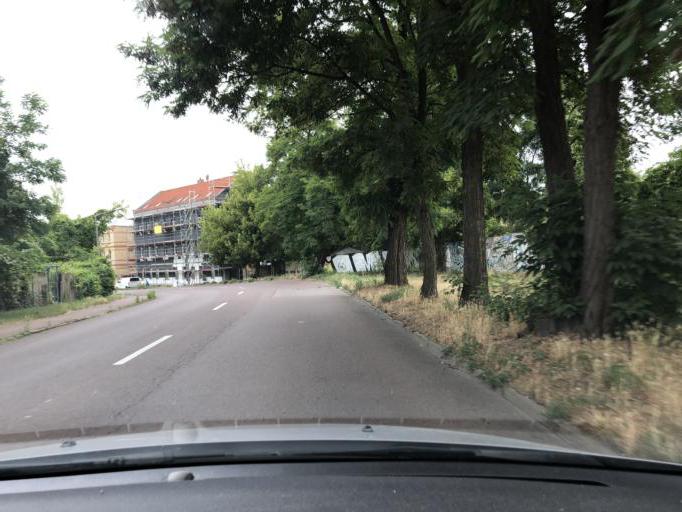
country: DE
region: Saxony-Anhalt
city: Schkopau
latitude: 51.4228
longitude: 12.0024
